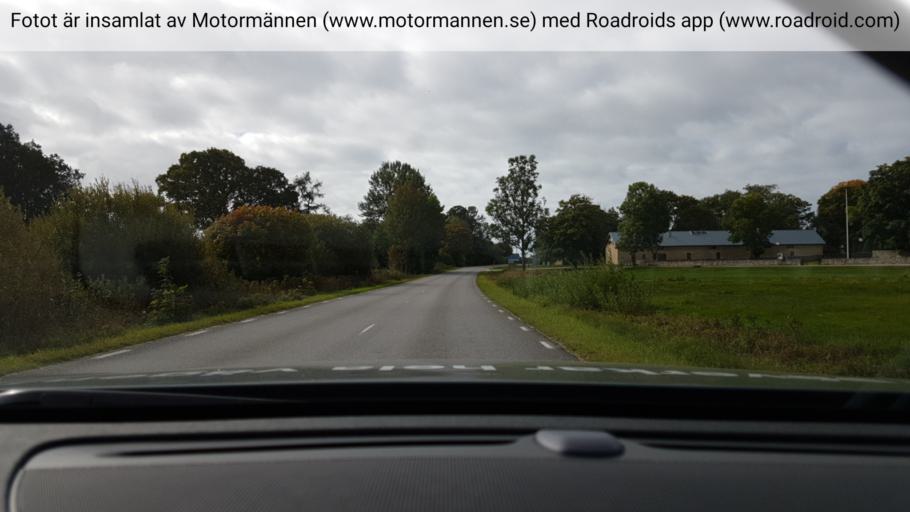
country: SE
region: Gotland
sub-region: Gotland
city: Hemse
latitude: 56.9704
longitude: 18.2334
